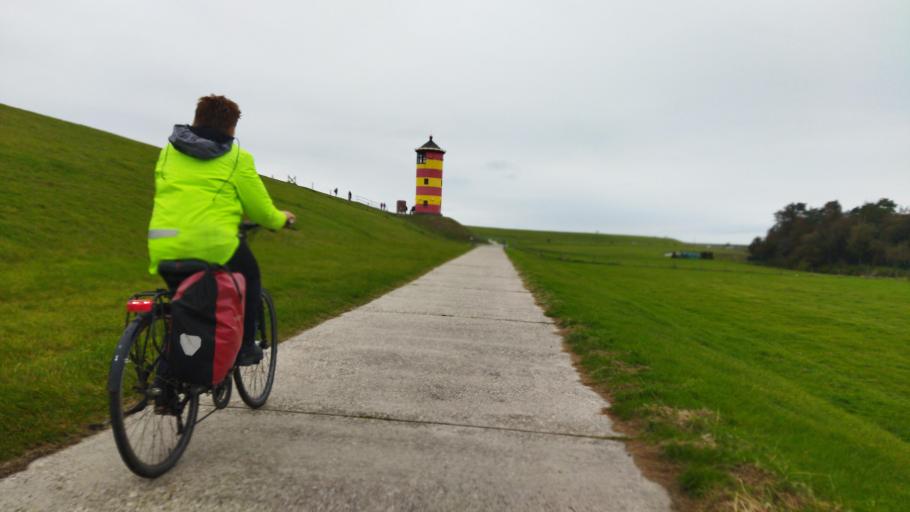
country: DE
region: Lower Saxony
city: Wirdum
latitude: 53.4969
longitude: 7.0451
